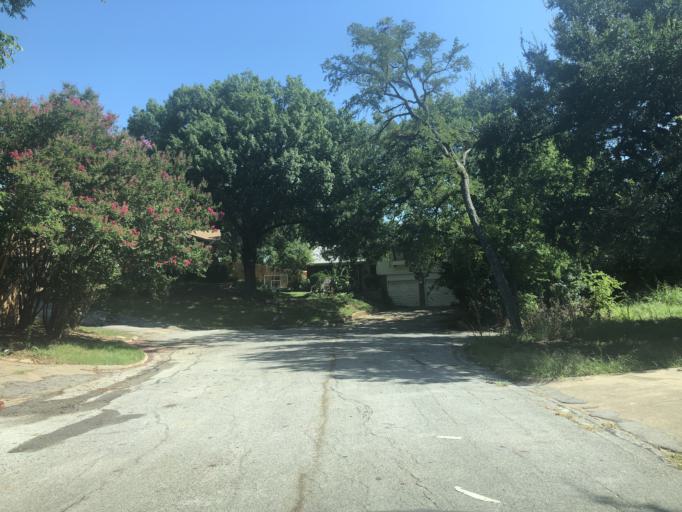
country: US
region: Texas
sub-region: Dallas County
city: Grand Prairie
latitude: 32.7513
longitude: -96.9999
